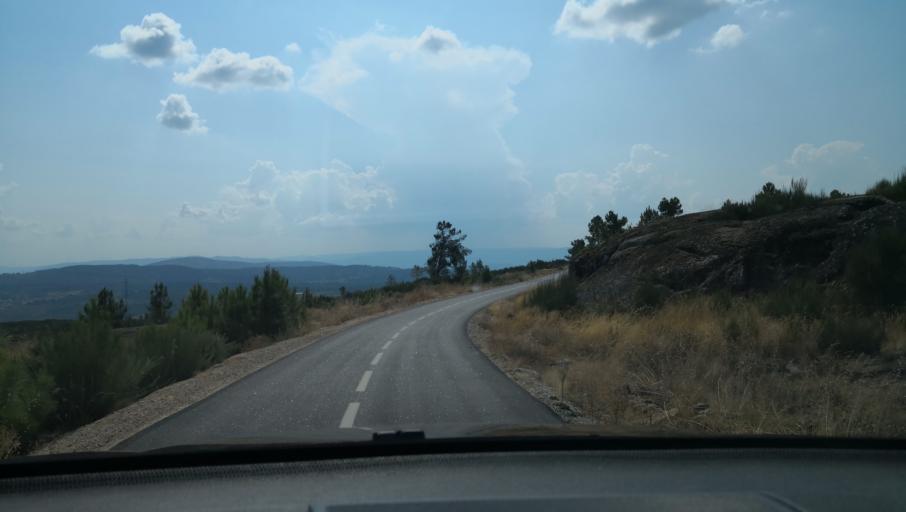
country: PT
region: Vila Real
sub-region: Sabrosa
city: Sabrosa
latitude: 41.2826
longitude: -7.6145
